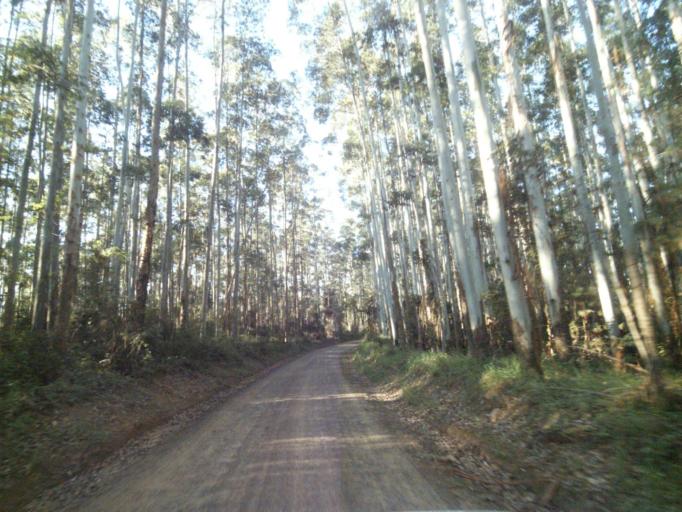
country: BR
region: Parana
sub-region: Telemaco Borba
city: Telemaco Borba
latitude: -24.5073
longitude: -50.6013
